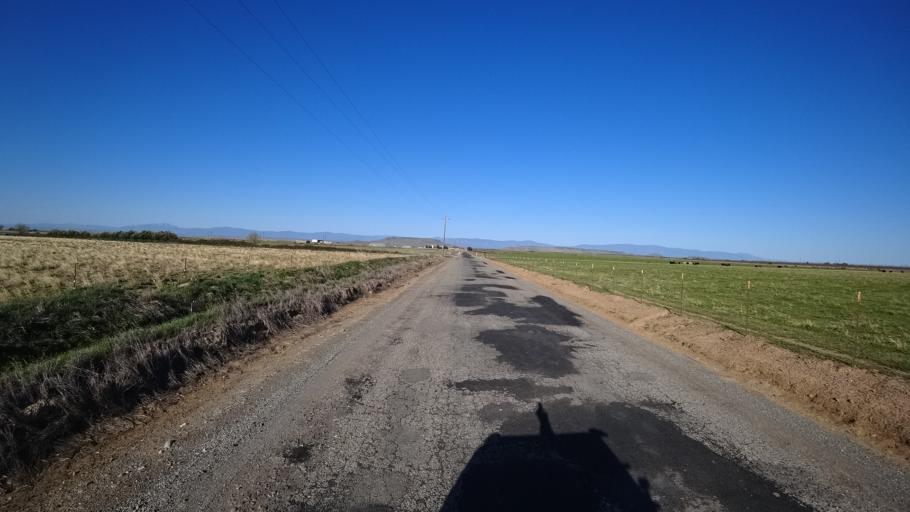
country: US
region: California
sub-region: Glenn County
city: Orland
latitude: 39.7589
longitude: -122.2508
